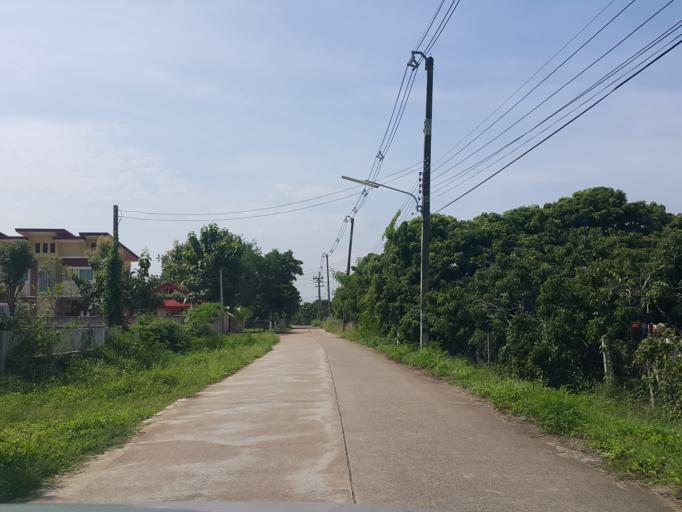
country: TH
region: Chiang Mai
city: Saraphi
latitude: 18.6844
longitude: 99.0683
